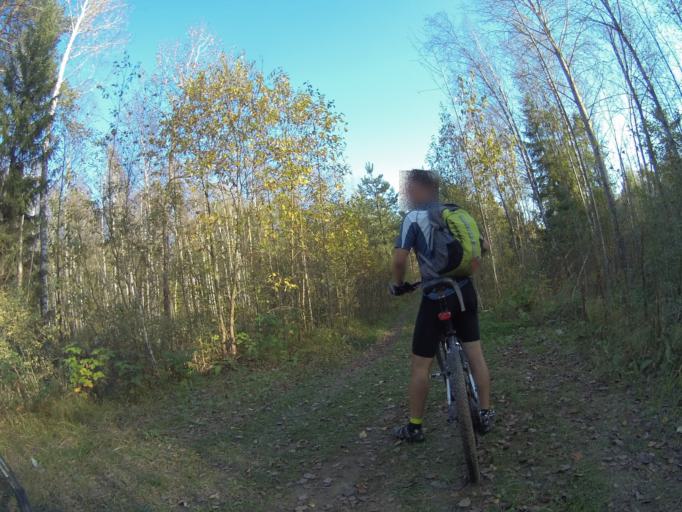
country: RU
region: Vladimir
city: Golovino
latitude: 56.0048
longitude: 40.4111
